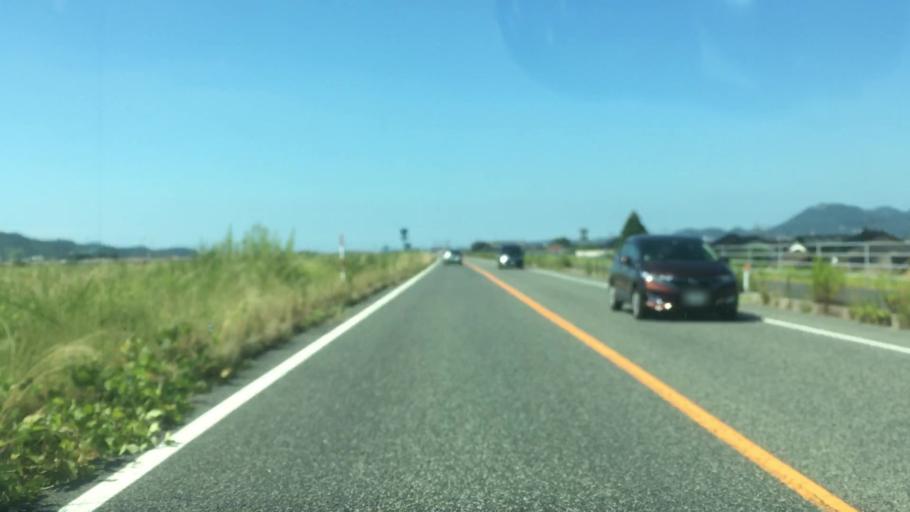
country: JP
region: Tottori
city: Tottori
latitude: 35.4571
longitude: 134.2152
